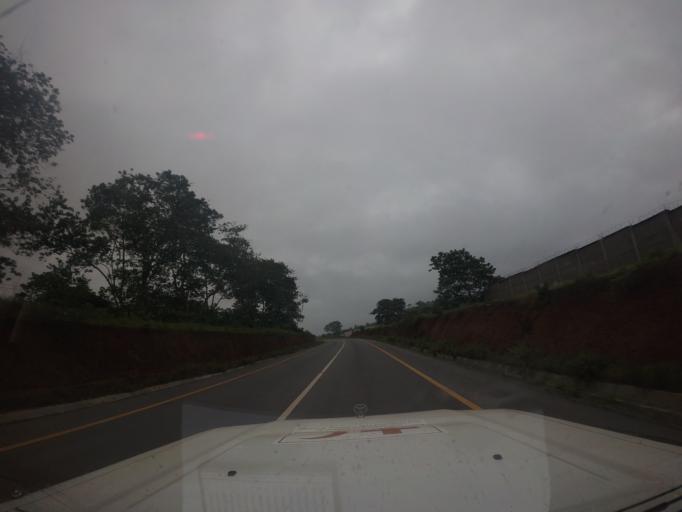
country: SL
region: Eastern Province
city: Hangha
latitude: 7.9229
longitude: -11.1534
